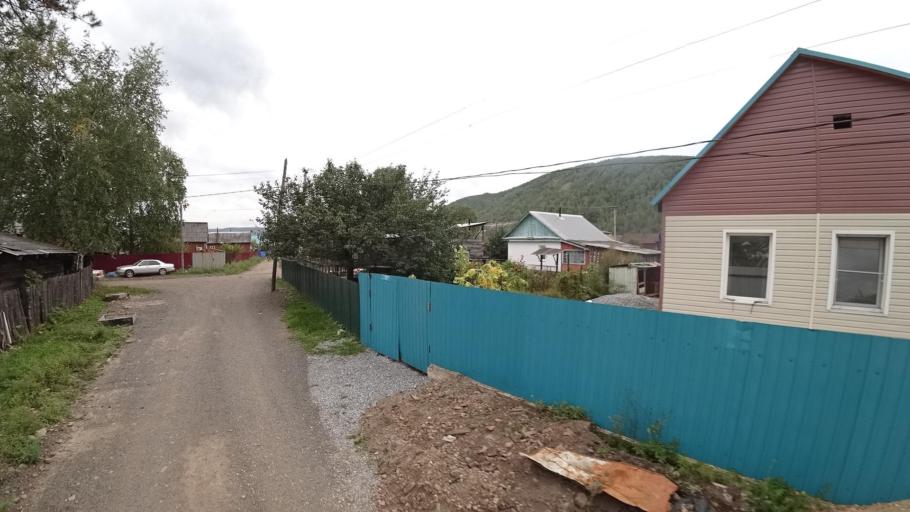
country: RU
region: Jewish Autonomous Oblast
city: Khingansk
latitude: 49.0049
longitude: 131.0496
